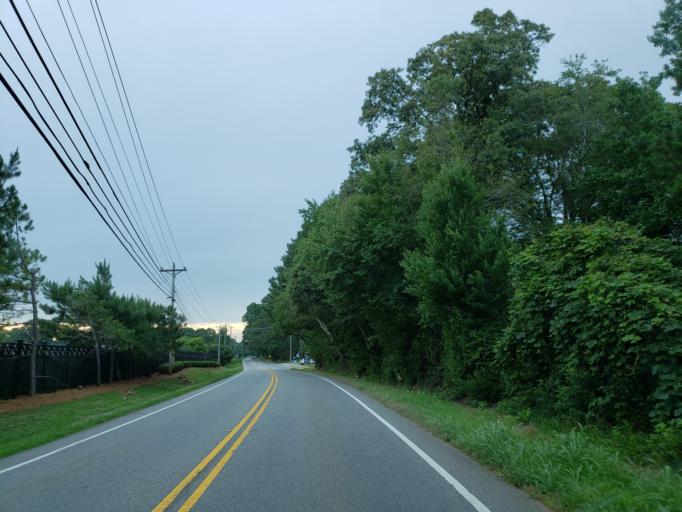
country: US
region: Georgia
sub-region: Cherokee County
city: Ball Ground
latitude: 34.2430
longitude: -84.3532
